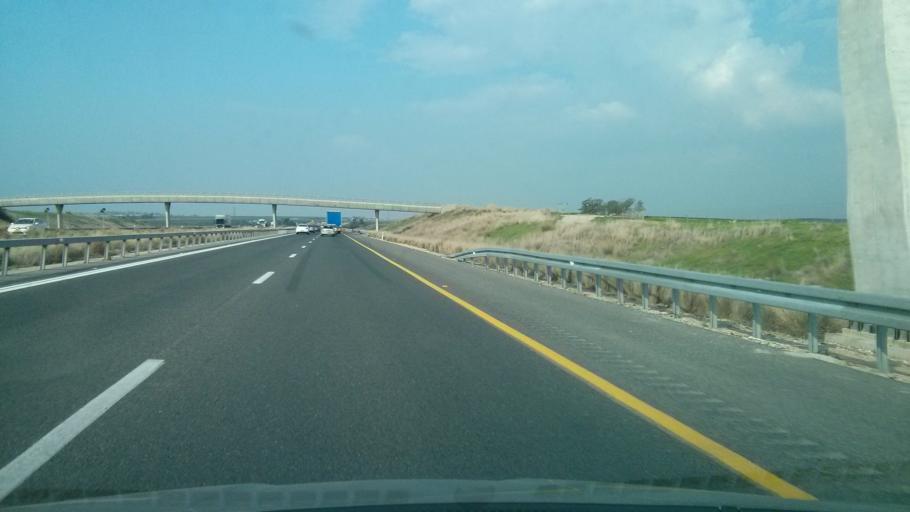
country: IL
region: Central District
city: Bene 'Ayish
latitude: 31.7362
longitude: 34.8222
